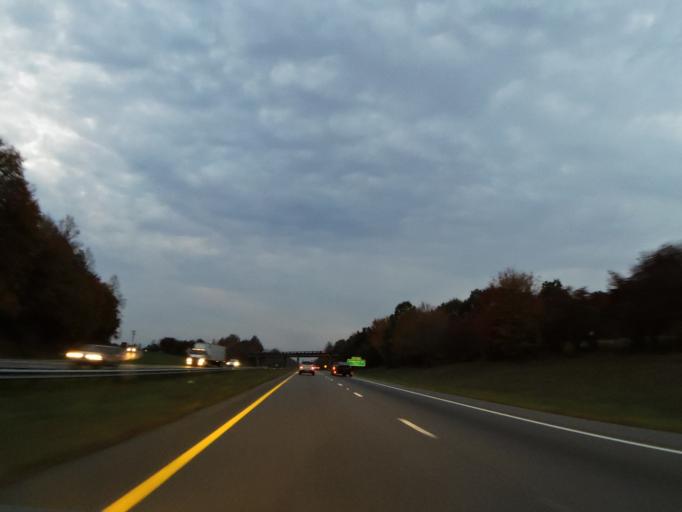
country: US
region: North Carolina
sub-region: McDowell County
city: West Marion
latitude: 35.6454
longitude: -81.9841
